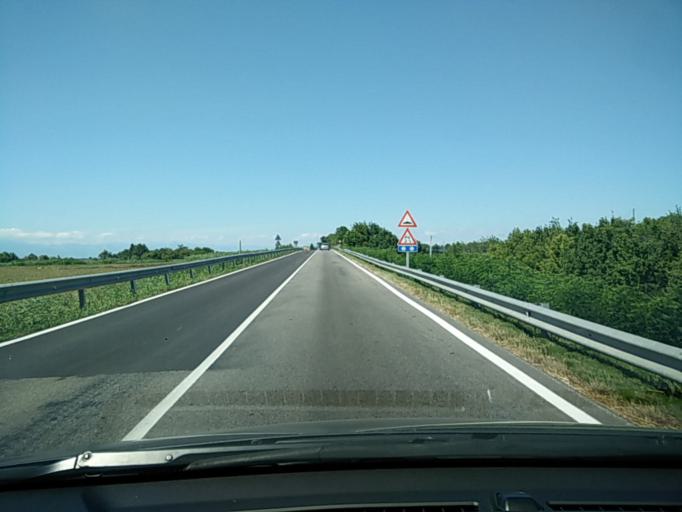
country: IT
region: Veneto
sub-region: Provincia di Venezia
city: La Salute di Livenza
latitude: 45.6882
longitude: 12.8447
